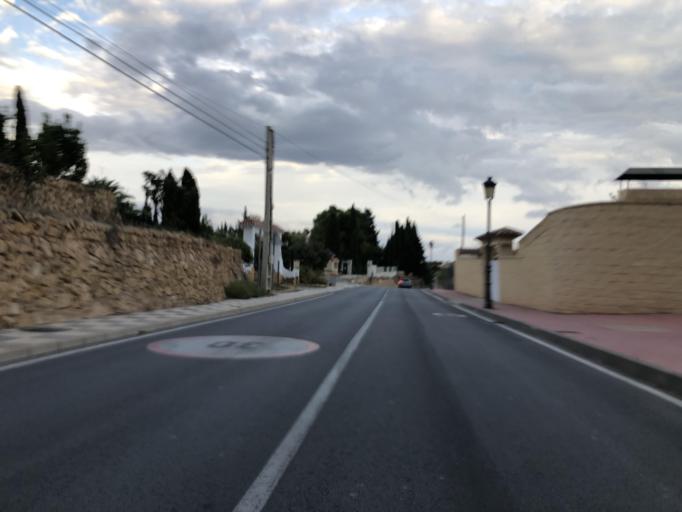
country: ES
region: Valencia
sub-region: Provincia de Alicante
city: Polop
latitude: 38.6247
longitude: -0.1348
